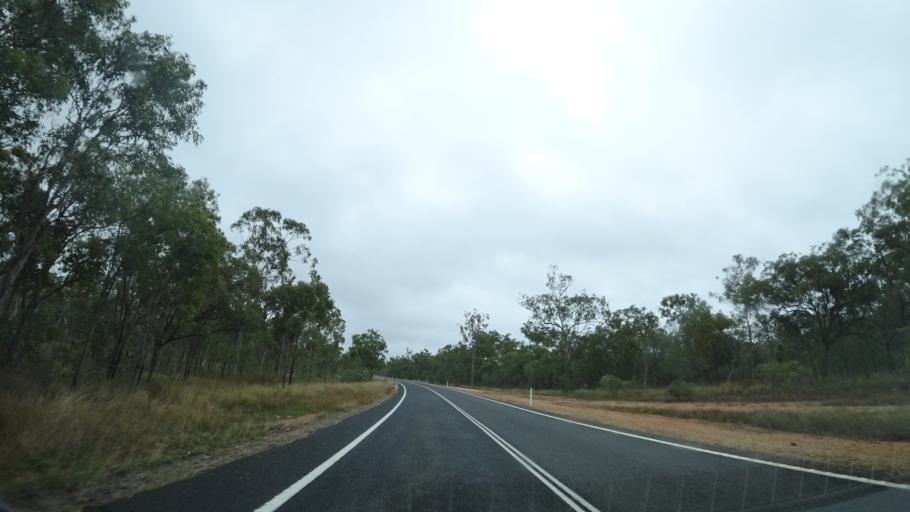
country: AU
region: Queensland
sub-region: Tablelands
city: Ravenshoe
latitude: -17.6867
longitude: 145.1440
